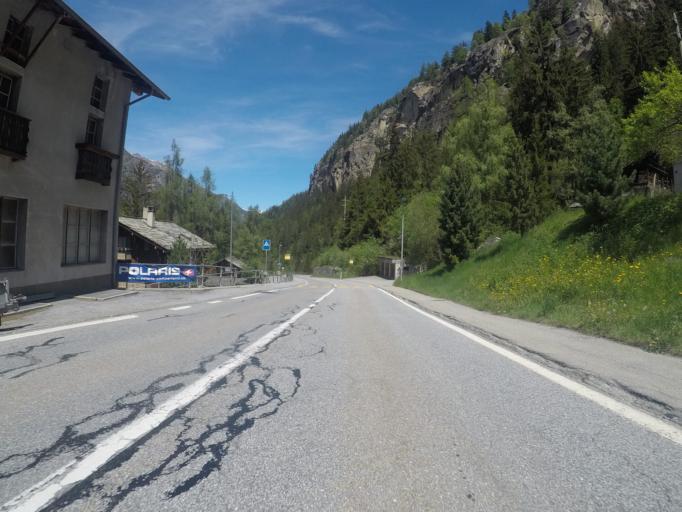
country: CH
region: Valais
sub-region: Visp District
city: Sankt Niklaus
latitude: 46.1617
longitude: 7.7982
